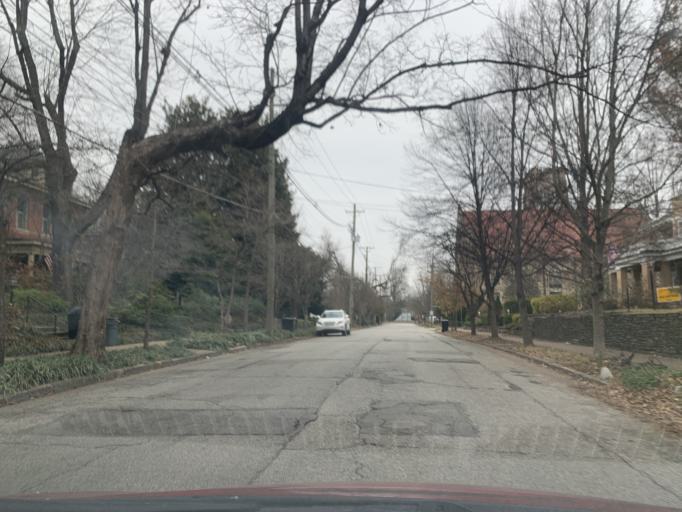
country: US
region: Kentucky
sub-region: Jefferson County
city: Indian Hills
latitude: 38.2520
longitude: -85.6976
